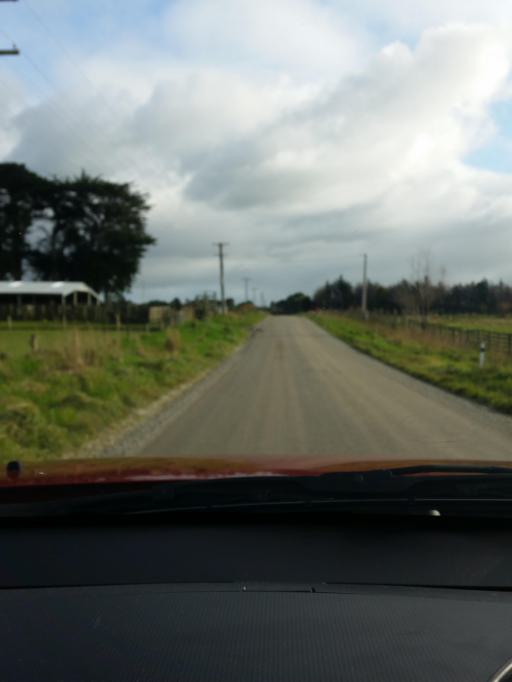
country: NZ
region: Southland
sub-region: Invercargill City
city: Invercargill
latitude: -46.3557
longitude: 168.4413
